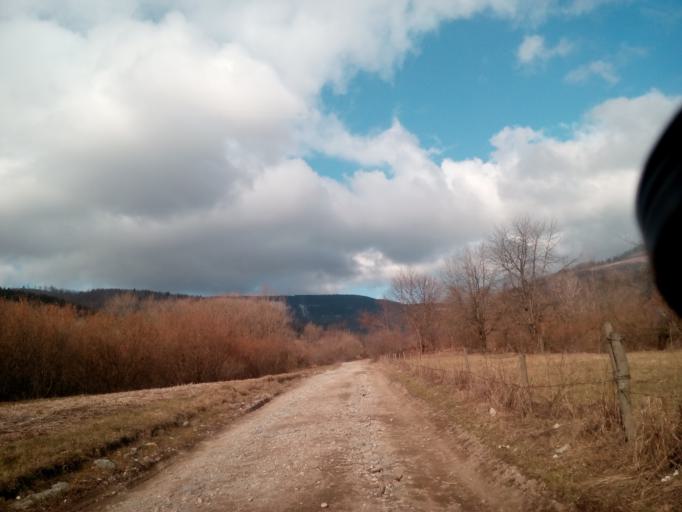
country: SK
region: Banskobystricky
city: Revuca
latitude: 48.7253
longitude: 20.2455
